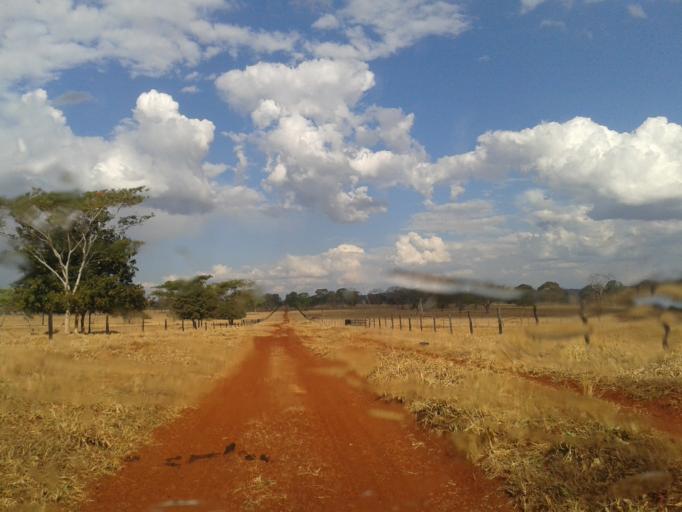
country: BR
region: Minas Gerais
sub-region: Santa Vitoria
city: Santa Vitoria
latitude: -19.1730
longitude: -49.9911
